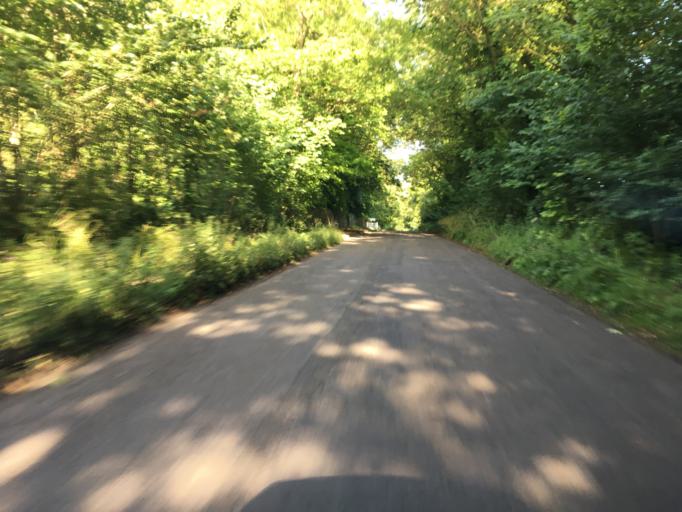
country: GB
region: England
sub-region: Oxfordshire
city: Burford
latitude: 51.8092
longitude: -1.6450
